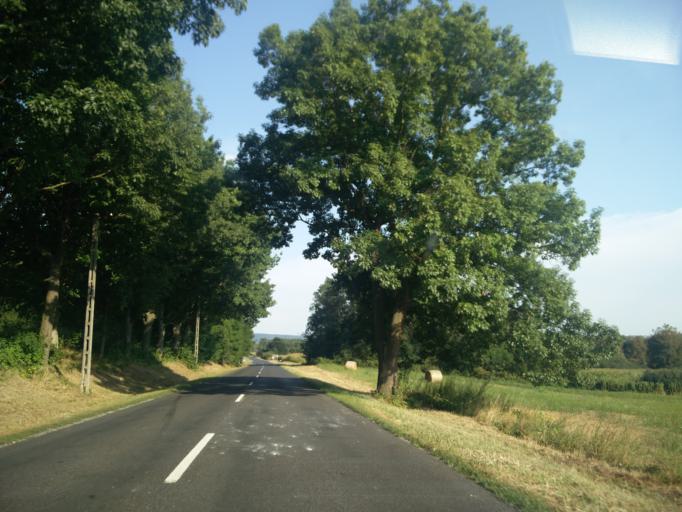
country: HU
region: Zala
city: Zalaegerszeg
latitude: 46.8603
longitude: 16.8131
